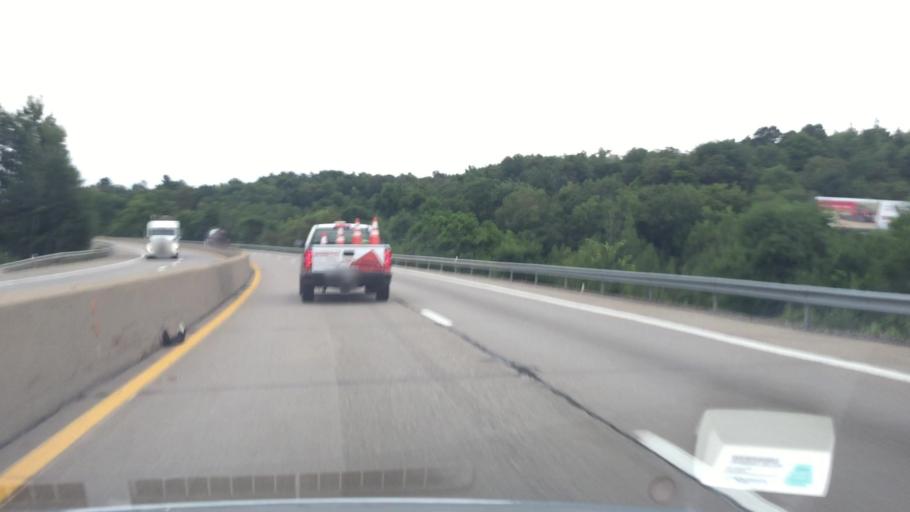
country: US
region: Pennsylvania
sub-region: Allegheny County
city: Imperial
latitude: 40.4233
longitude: -80.3033
